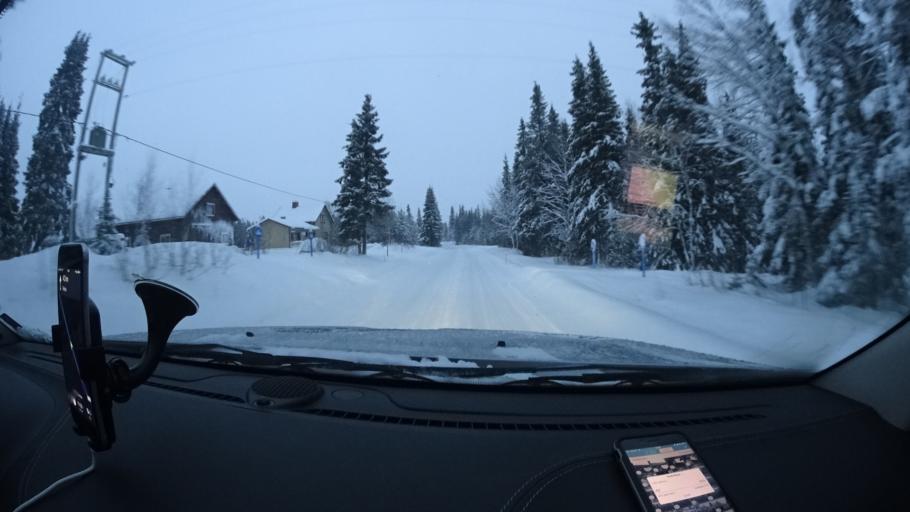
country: FI
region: Lapland
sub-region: Tunturi-Lappi
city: Kittilae
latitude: 67.9257
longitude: 25.0491
